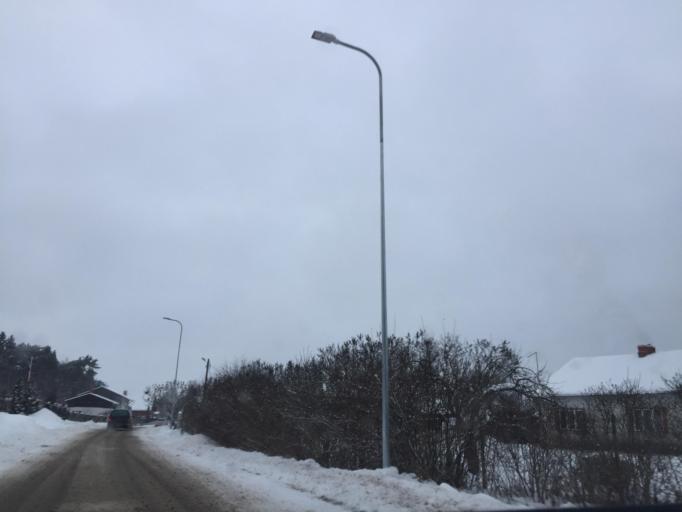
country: LV
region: Smiltene
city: Smiltene
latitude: 57.4146
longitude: 25.8955
